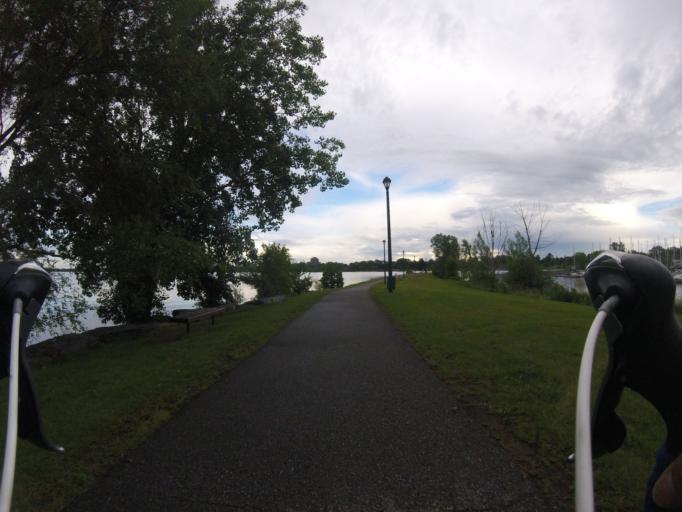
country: CA
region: Ontario
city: Bells Corners
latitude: 45.3541
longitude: -75.8263
